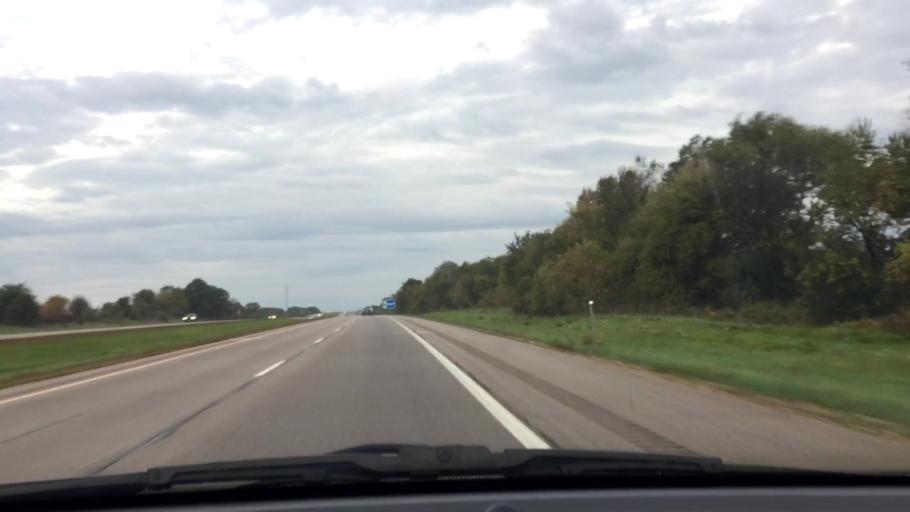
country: US
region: Wisconsin
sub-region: Rock County
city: Clinton
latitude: 42.5729
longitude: -88.8498
